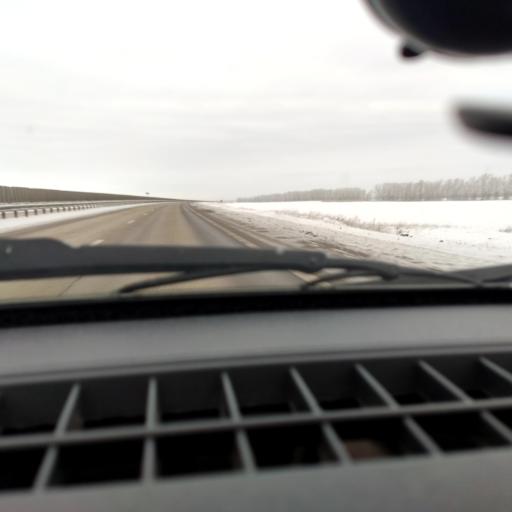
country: RU
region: Bashkortostan
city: Kushnarenkovo
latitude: 55.0875
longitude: 55.2555
